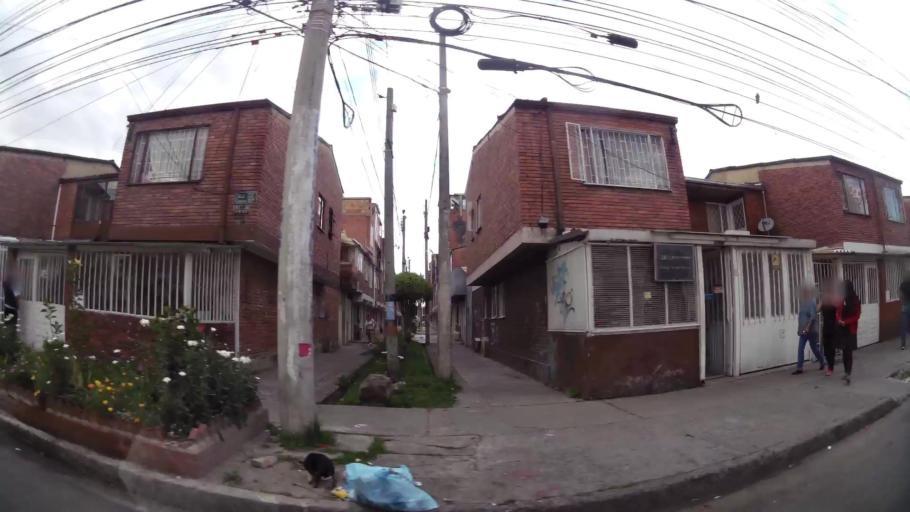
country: CO
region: Cundinamarca
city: Cota
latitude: 4.7373
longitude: -74.0975
